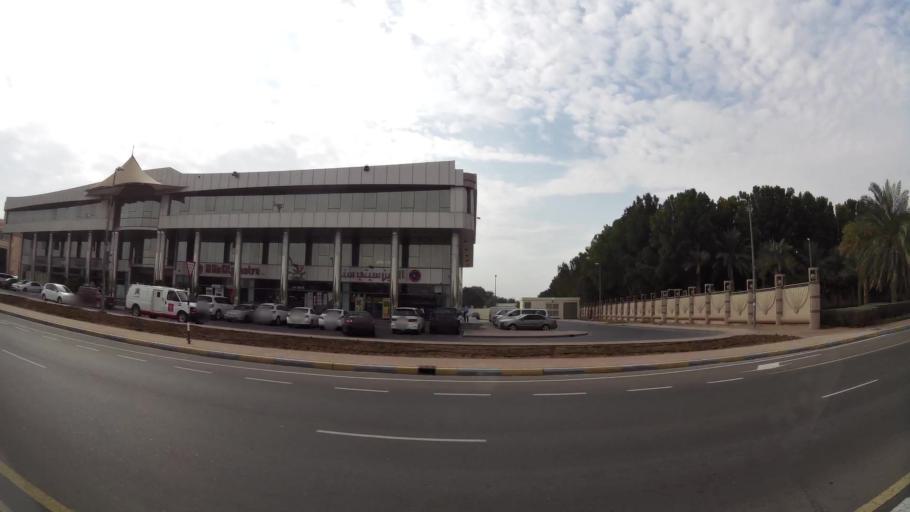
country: AE
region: Abu Dhabi
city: Al Ain
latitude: 24.2239
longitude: 55.7265
